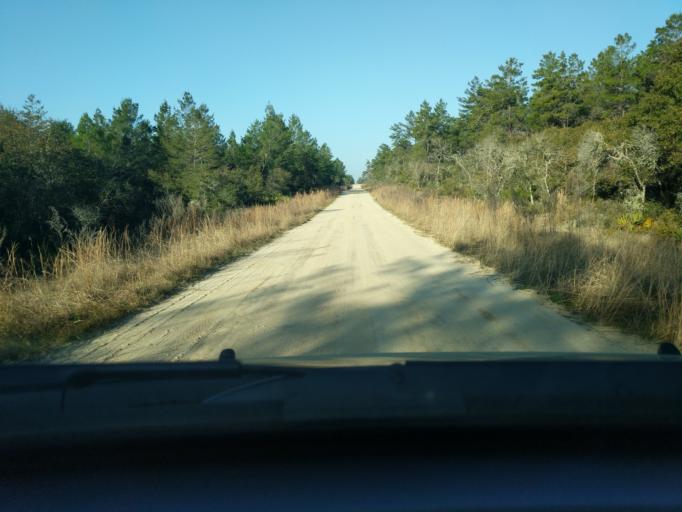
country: US
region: Florida
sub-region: Marion County
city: Silver Springs Shores
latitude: 29.2263
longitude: -81.8067
